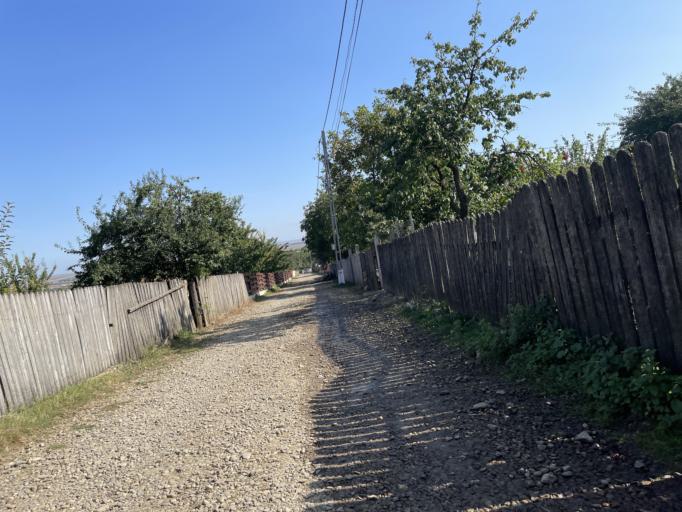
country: RO
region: Iasi
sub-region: Comuna Dumesti
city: Pausesti
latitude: 47.1520
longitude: 27.3174
